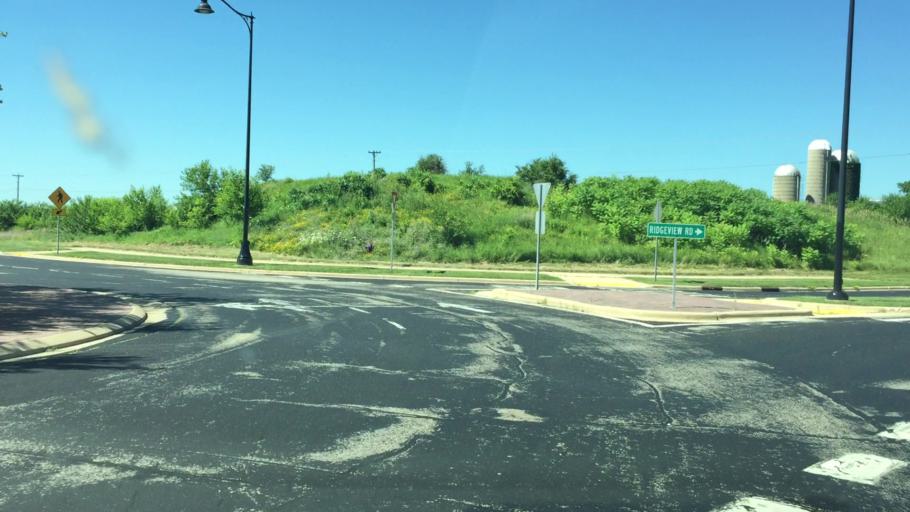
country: US
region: Wisconsin
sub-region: Dane County
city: Mount Horeb
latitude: 43.0065
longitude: -89.7037
